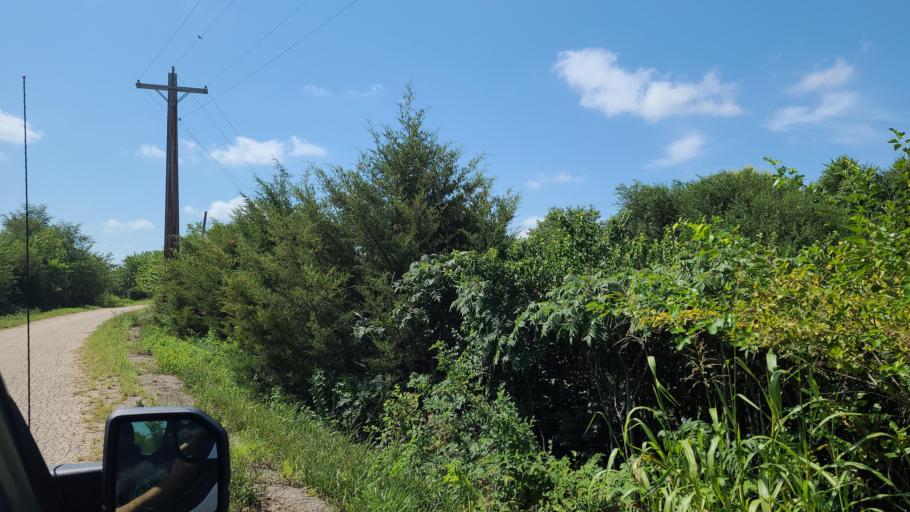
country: US
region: Kansas
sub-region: Douglas County
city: Lawrence
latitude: 38.9538
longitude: -95.1964
